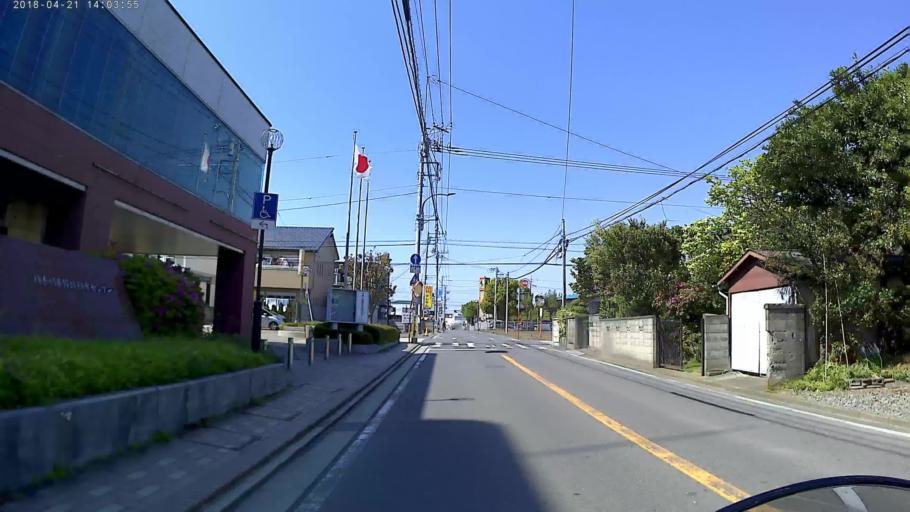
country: JP
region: Kanagawa
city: Hiratsuka
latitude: 35.3476
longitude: 139.3519
